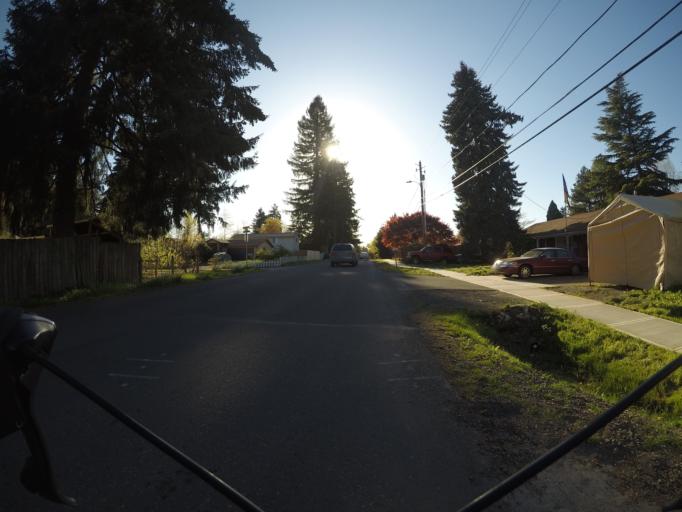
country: US
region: Oregon
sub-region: Washington County
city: Aloha
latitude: 45.4789
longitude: -122.8730
